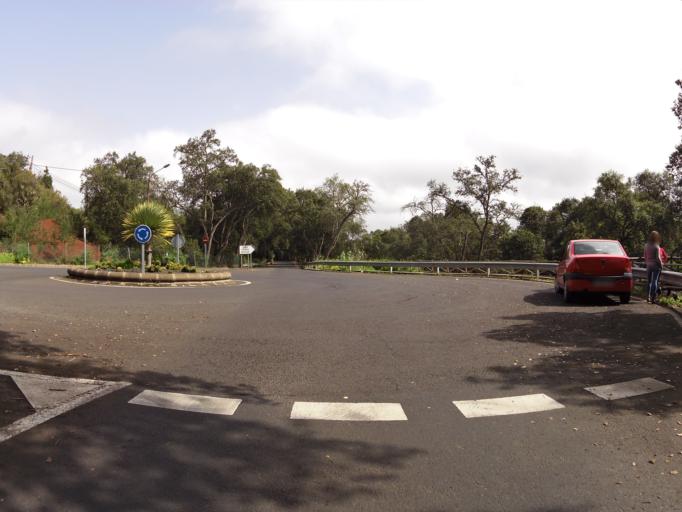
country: ES
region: Canary Islands
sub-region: Provincia de Las Palmas
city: Teror
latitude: 28.0680
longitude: -15.5430
